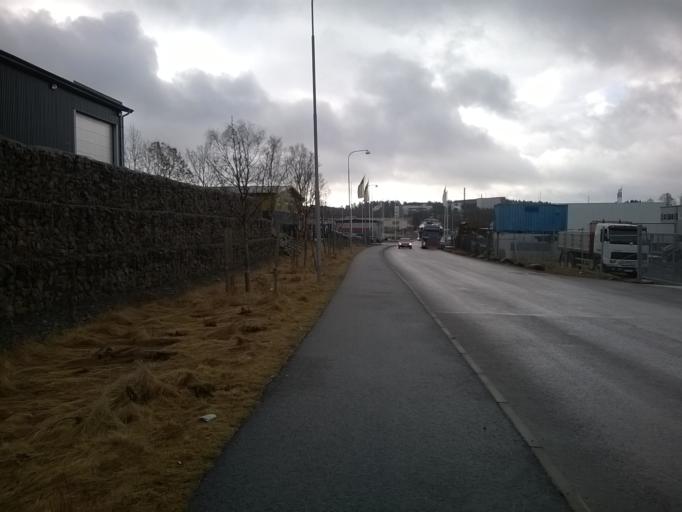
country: SE
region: Vaestra Goetaland
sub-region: Kungalvs Kommun
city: Kungalv
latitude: 57.8925
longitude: 11.9397
